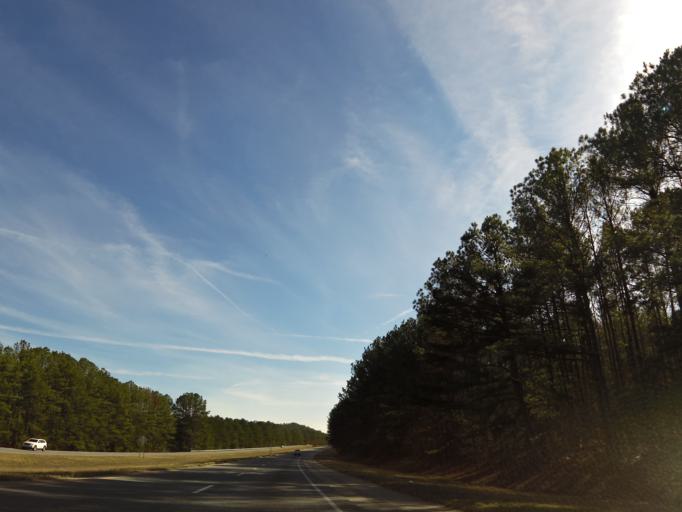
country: US
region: Georgia
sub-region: Harris County
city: Pine Mountain
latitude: 32.9304
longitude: -84.9491
